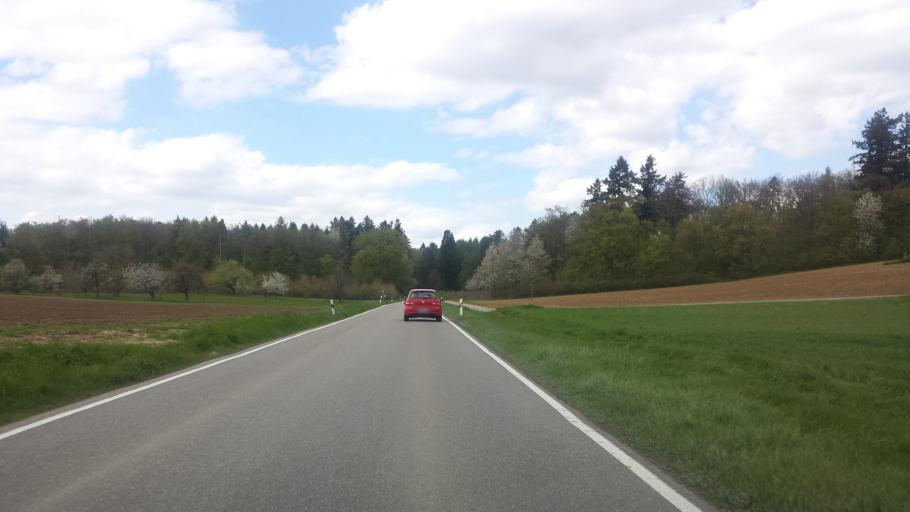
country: DE
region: Baden-Wuerttemberg
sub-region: Karlsruhe Region
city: Wiernsheim
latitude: 48.9127
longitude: 8.8467
